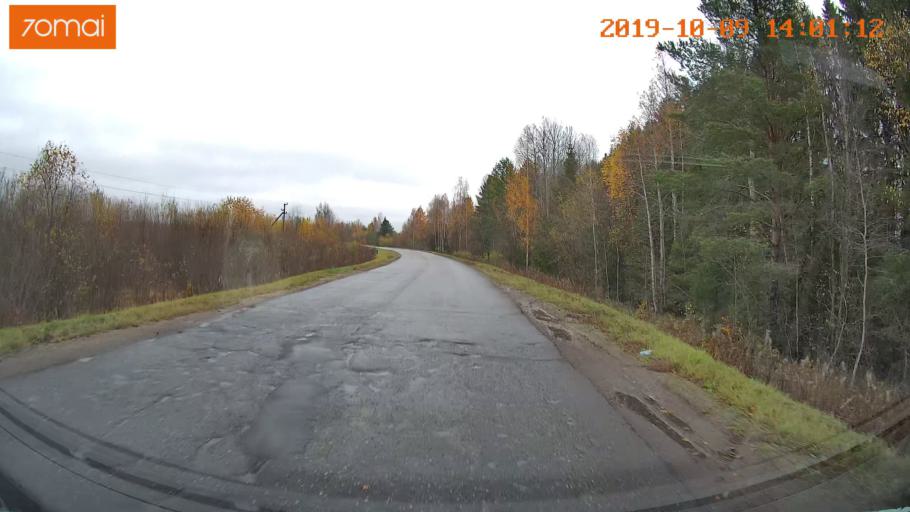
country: RU
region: Kostroma
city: Buy
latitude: 58.4420
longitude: 41.3447
